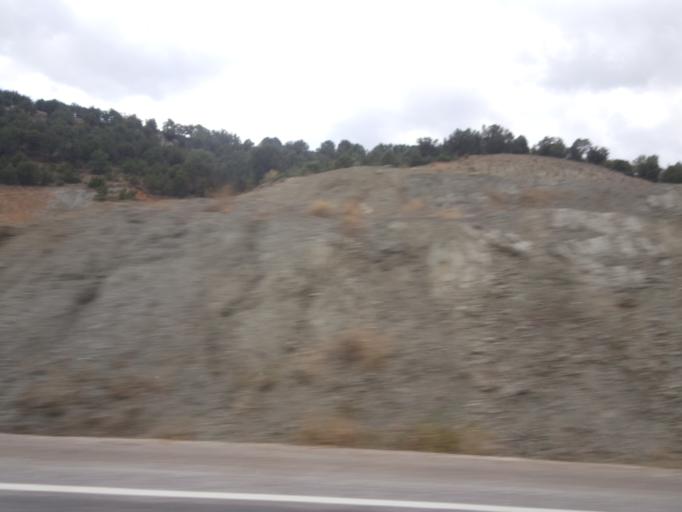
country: TR
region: Yozgat
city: Cekerek
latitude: 40.1893
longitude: 35.4436
